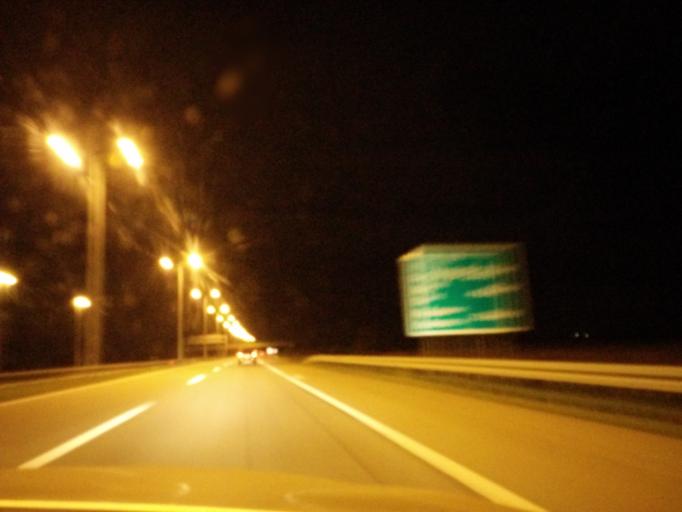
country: RS
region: Autonomna Pokrajina Vojvodina
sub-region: Sremski Okrug
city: Sremska Mitrovica
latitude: 44.9991
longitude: 19.6467
